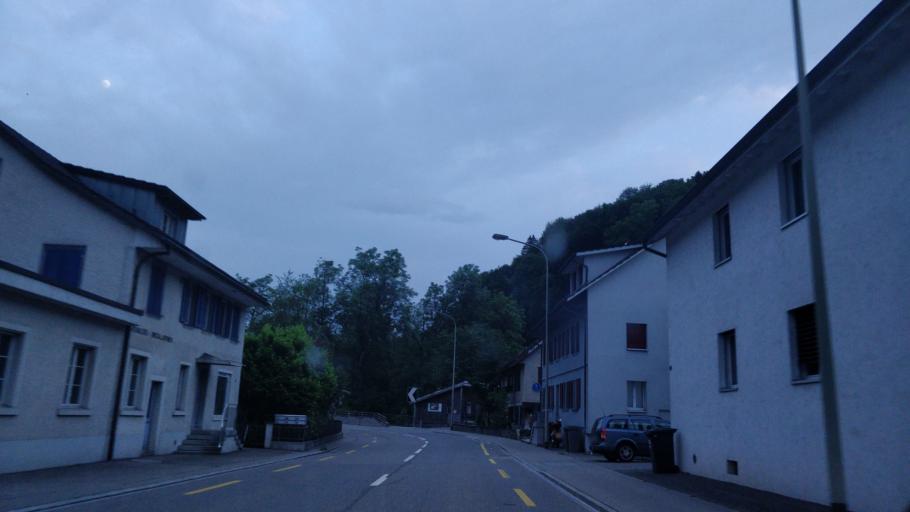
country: CH
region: Zurich
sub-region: Bezirk Buelach
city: Rorbas
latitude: 47.5262
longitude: 8.5786
